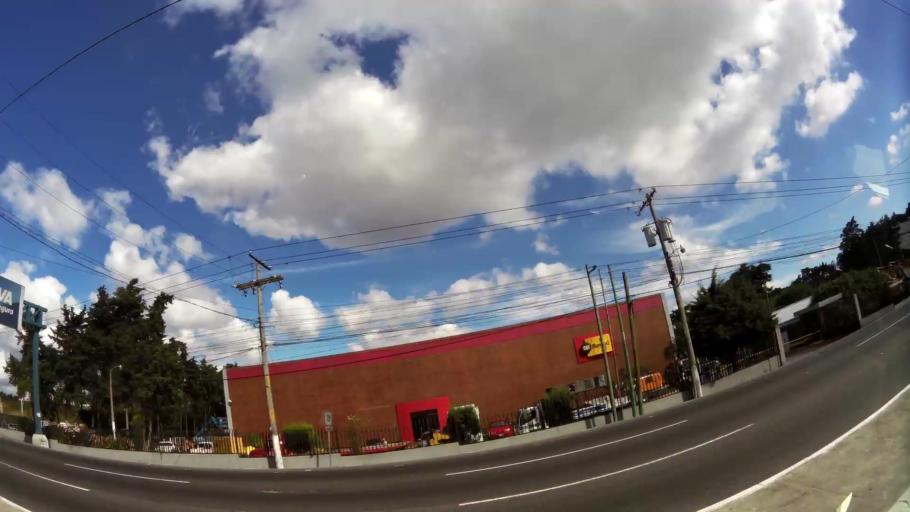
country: GT
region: Guatemala
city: Villa Nueva
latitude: 14.5696
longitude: -90.5738
